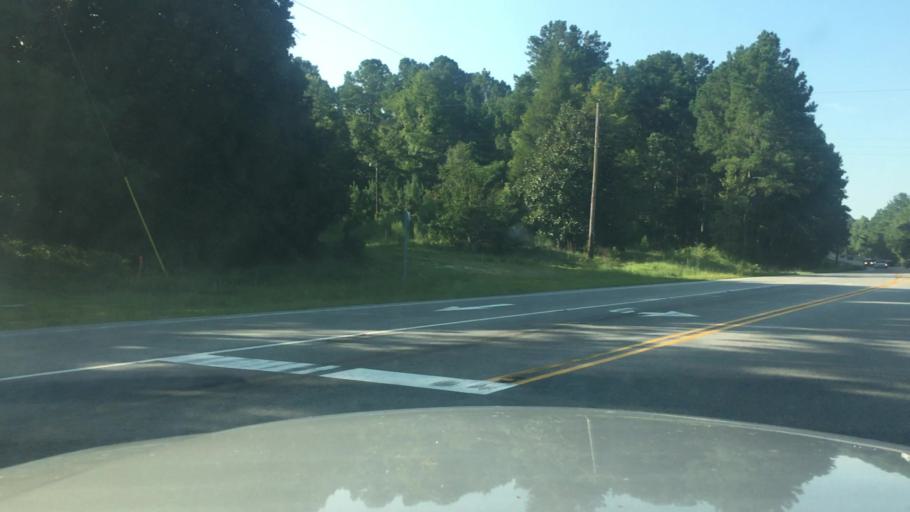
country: US
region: North Carolina
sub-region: Harnett County
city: Walkertown
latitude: 35.2053
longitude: -78.8491
